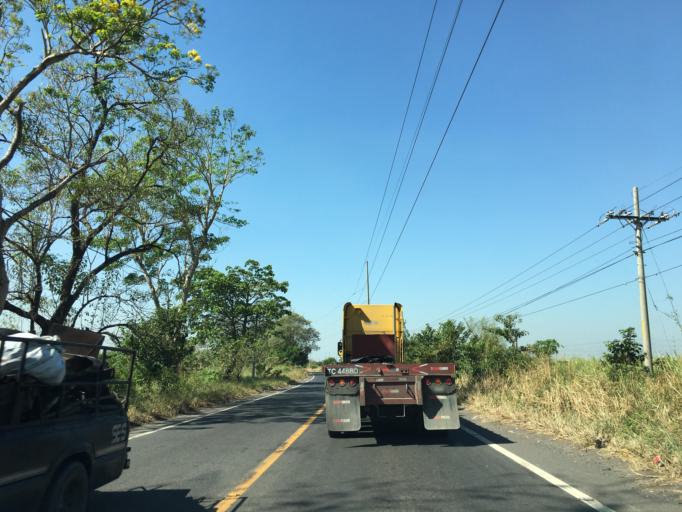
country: GT
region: Escuintla
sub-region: Municipio de Masagua
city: Masagua
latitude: 14.2447
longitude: -90.8120
